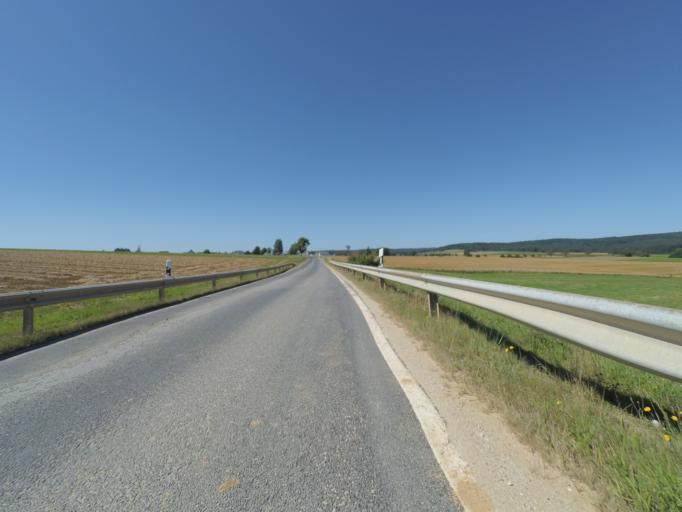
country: DE
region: Rheinland-Pfalz
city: Grosslittgen
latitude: 50.0300
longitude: 6.8075
